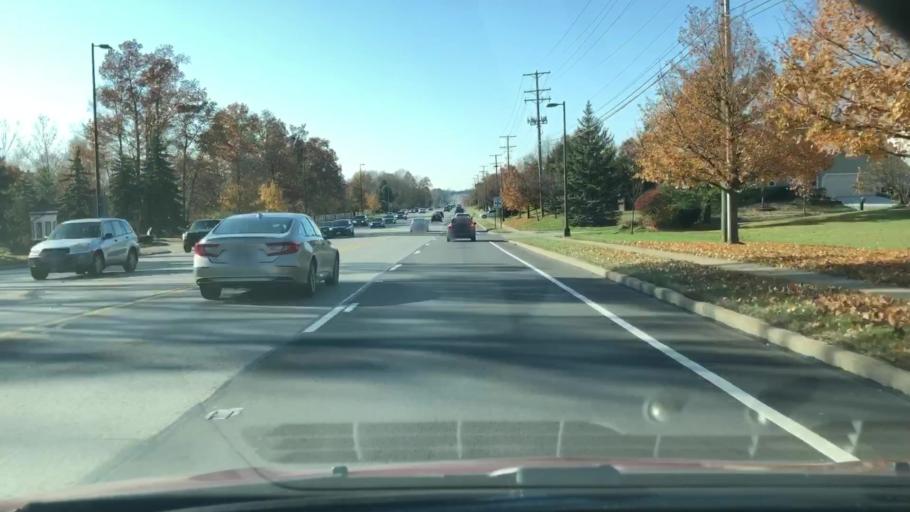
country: US
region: Ohio
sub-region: Franklin County
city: Gahanna
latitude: 40.0559
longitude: -82.8755
